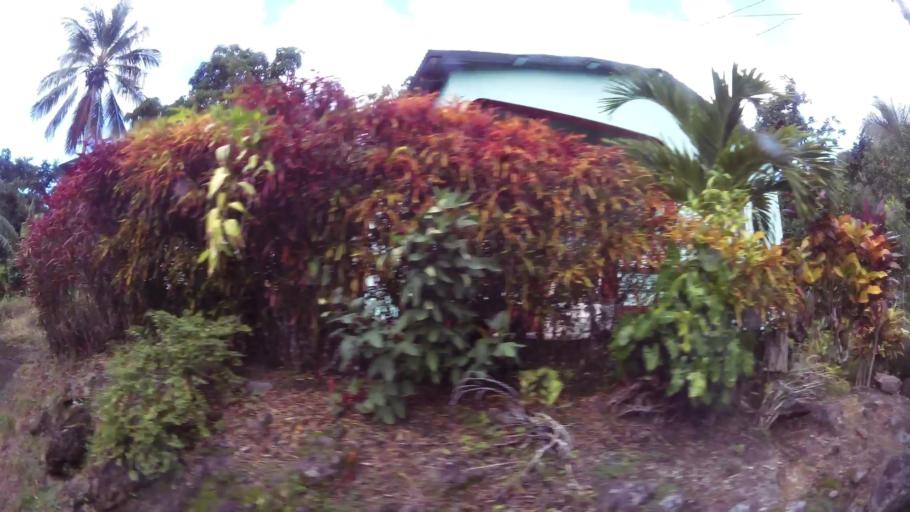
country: DM
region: Saint John
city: Portsmouth
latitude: 15.6212
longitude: -61.4599
